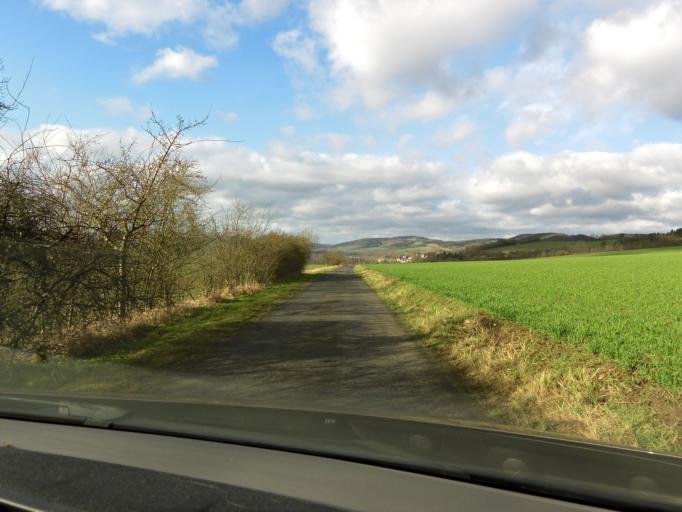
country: DE
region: Thuringia
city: Krauthausen
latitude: 51.0409
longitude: 10.2690
